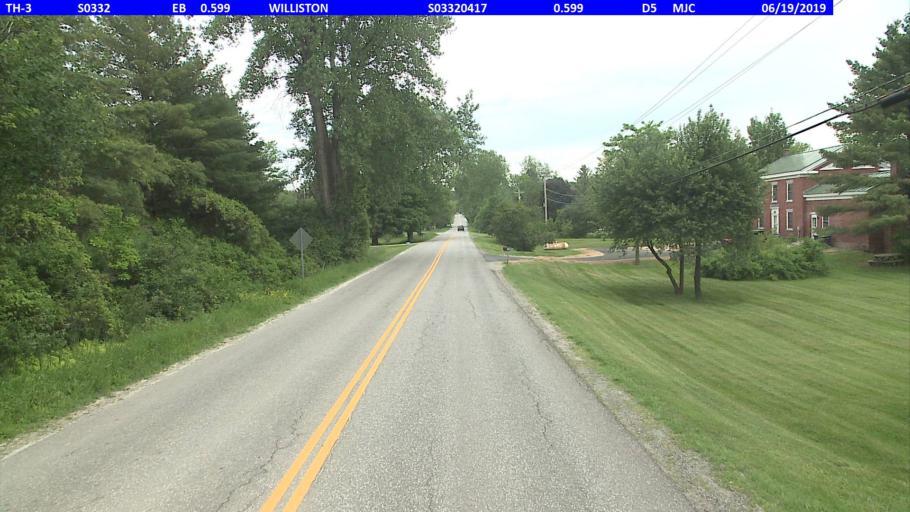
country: US
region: Vermont
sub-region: Chittenden County
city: Williston
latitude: 44.4239
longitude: -73.1111
